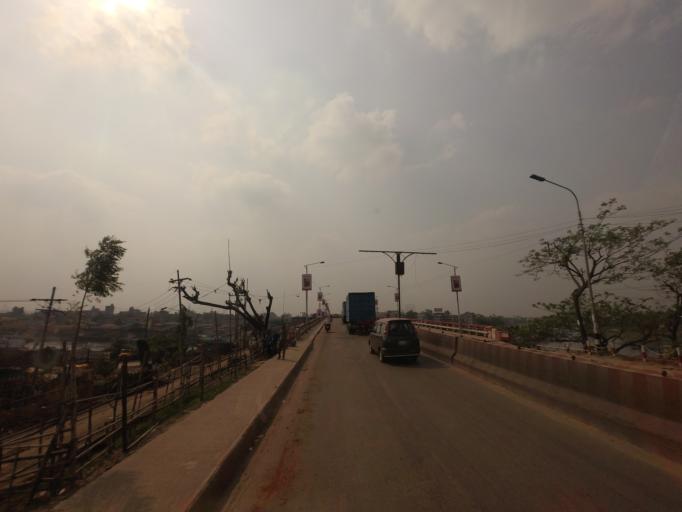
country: BD
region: Dhaka
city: Azimpur
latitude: 23.7837
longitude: 90.3366
